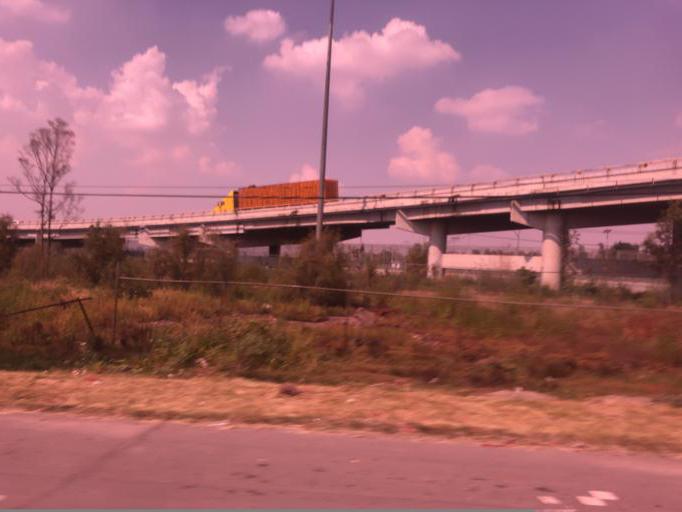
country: MX
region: Mexico
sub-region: Ciudad Nezahualcoyotl
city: Colonia Gustavo Baz Prada
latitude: 19.4688
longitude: -99.0067
